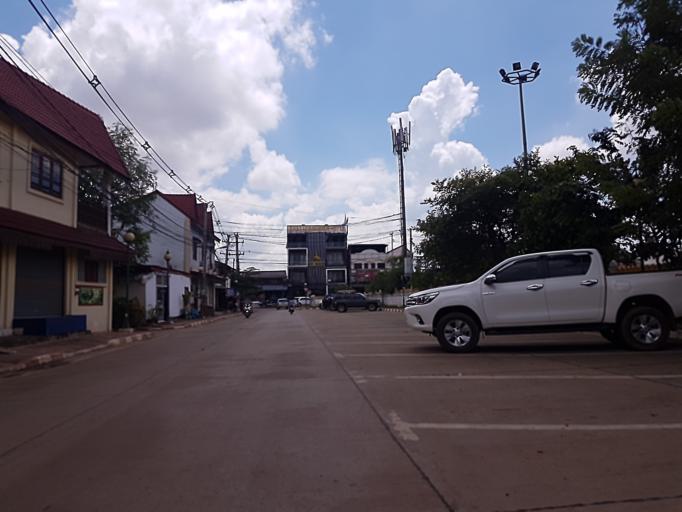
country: LA
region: Vientiane
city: Vientiane
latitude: 17.9761
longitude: 102.6375
